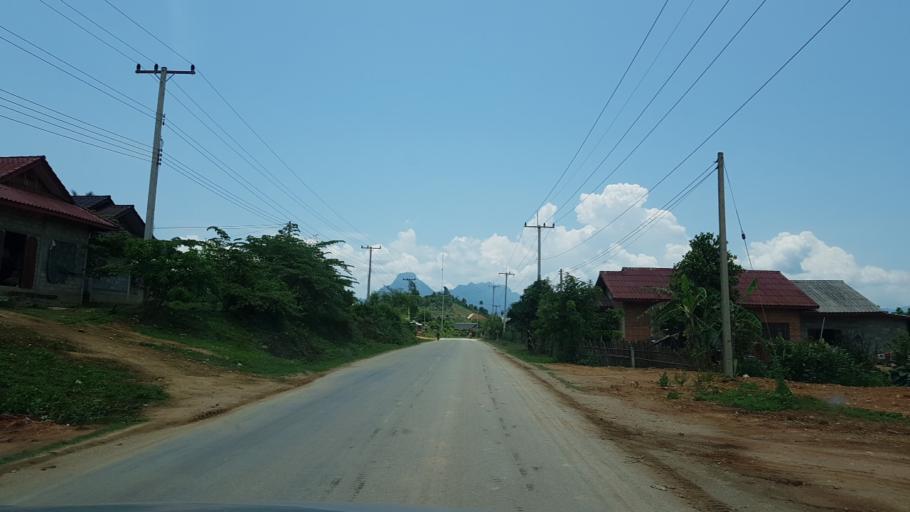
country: LA
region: Vientiane
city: Muang Kasi
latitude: 19.2721
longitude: 102.2253
